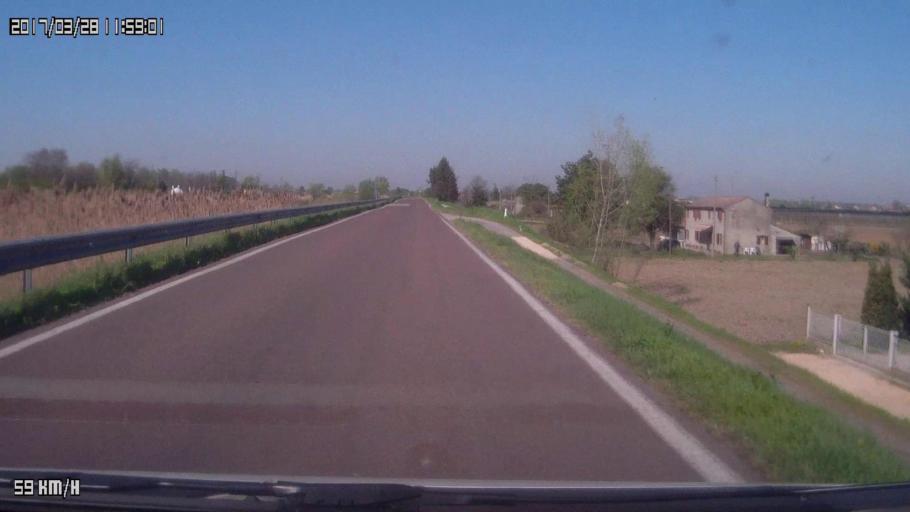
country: IT
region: Veneto
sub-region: Provincia di Venezia
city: Boscochiaro
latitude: 45.1412
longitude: 12.1094
